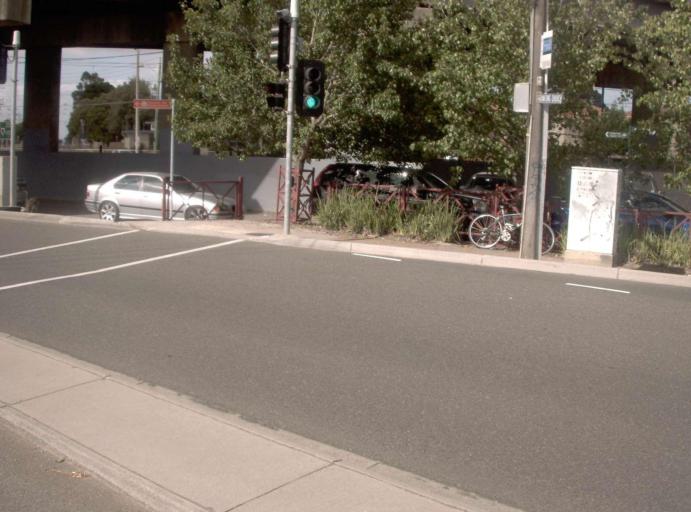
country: AU
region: Victoria
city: Clayton
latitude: -37.9114
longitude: 145.1035
